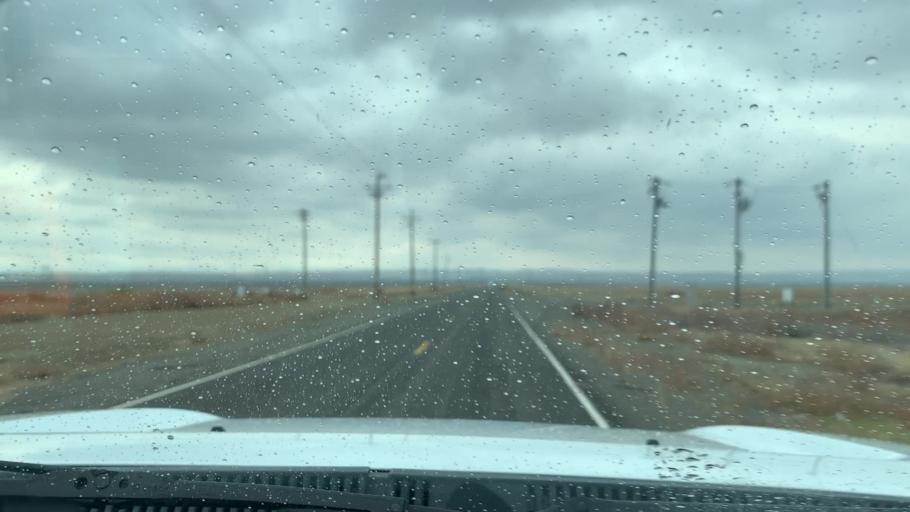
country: US
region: California
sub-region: Kings County
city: Kettleman City
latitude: 35.9343
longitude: -119.8781
